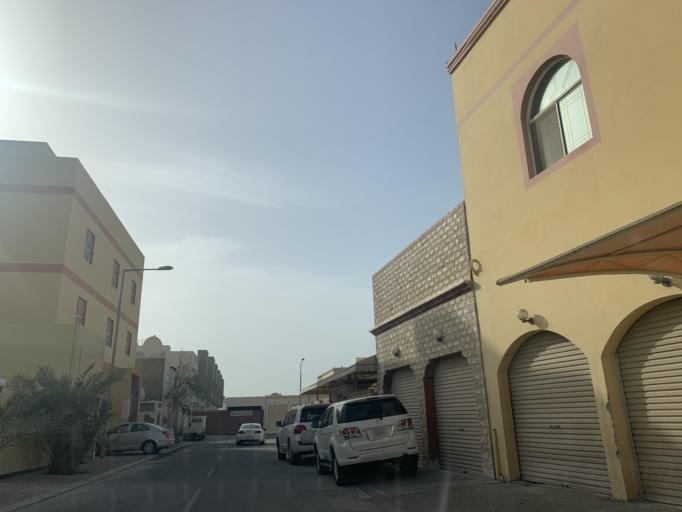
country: BH
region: Northern
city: Madinat `Isa
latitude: 26.1577
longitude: 50.5110
